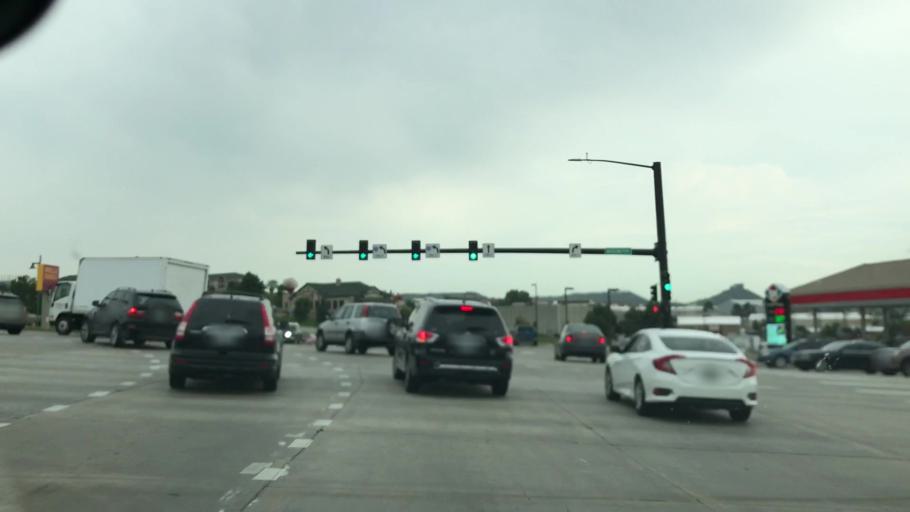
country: US
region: Colorado
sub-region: Douglas County
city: Castle Rock
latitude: 39.4109
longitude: -104.8722
